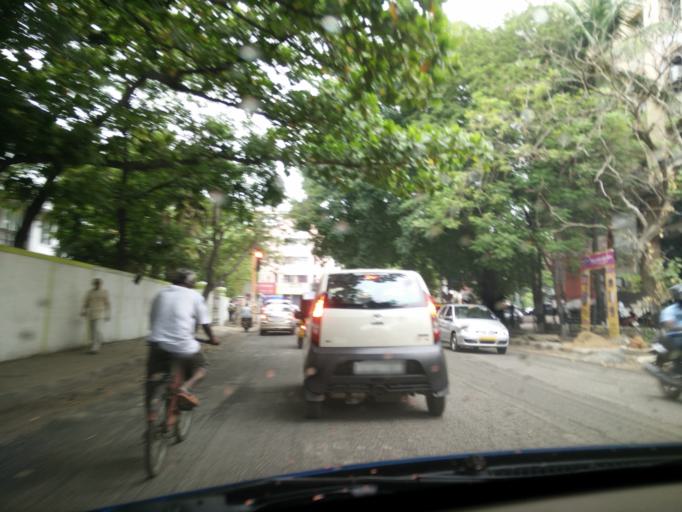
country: IN
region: Tamil Nadu
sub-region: Chennai
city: Gandhi Nagar
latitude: 13.0061
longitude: 80.2516
